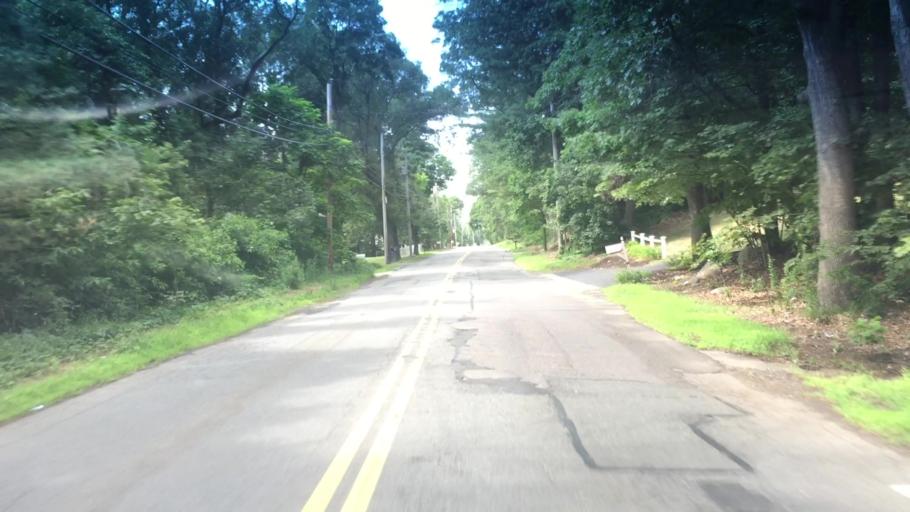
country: US
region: Massachusetts
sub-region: Norfolk County
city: Medway
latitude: 42.1291
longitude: -71.3996
